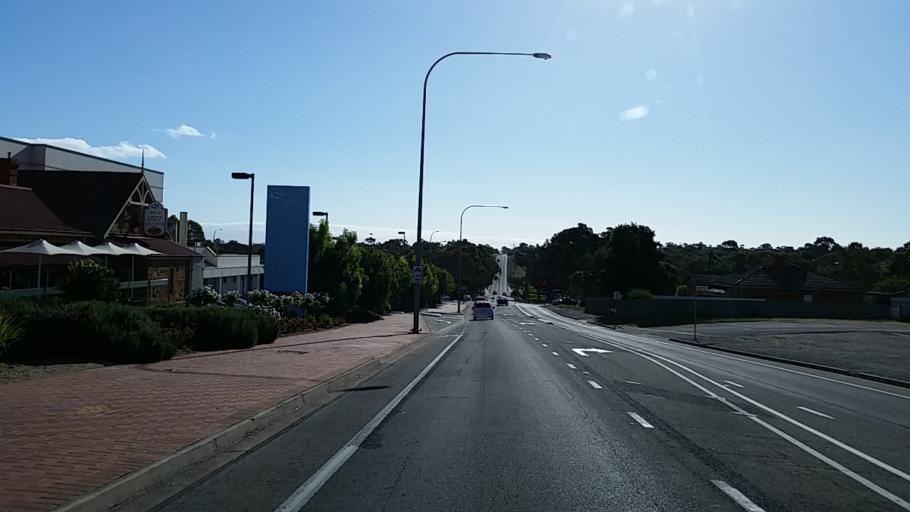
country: AU
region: South Australia
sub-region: Tea Tree Gully
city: Modbury
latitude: -34.8280
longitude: 138.6891
